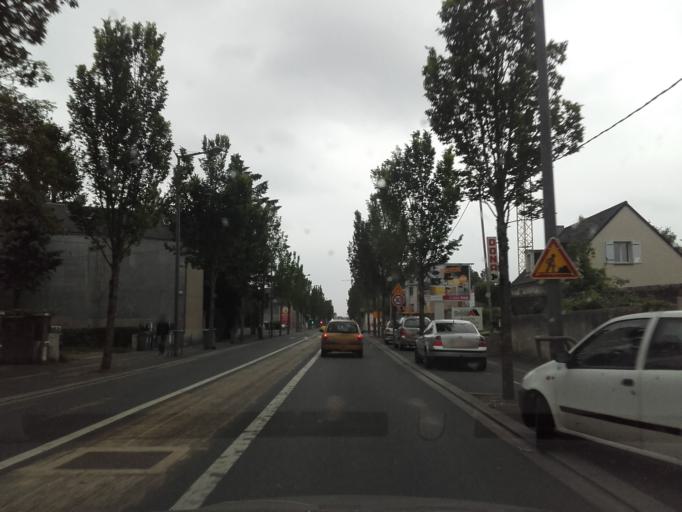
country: FR
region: Centre
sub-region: Departement d'Indre-et-Loire
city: Saint-Cyr-sur-Loire
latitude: 47.4167
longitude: 0.6903
